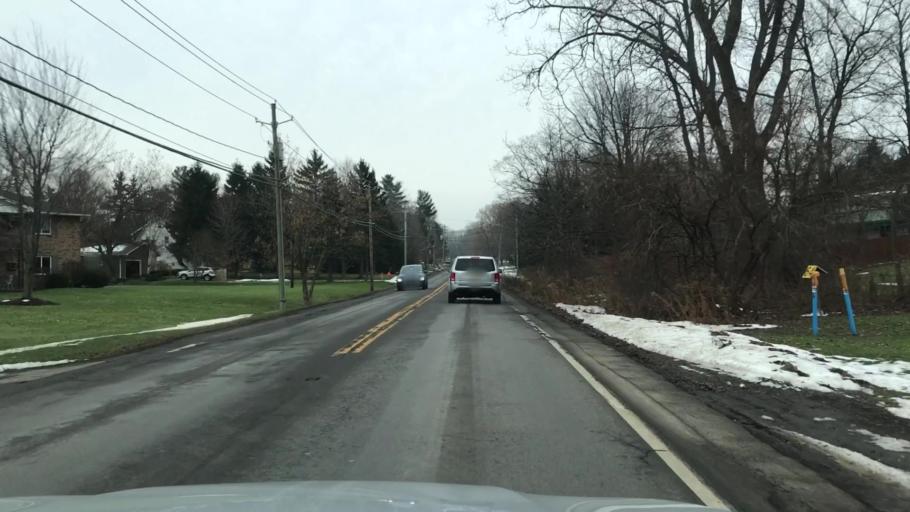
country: US
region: New York
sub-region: Erie County
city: Hamburg
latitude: 42.7405
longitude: -78.7944
